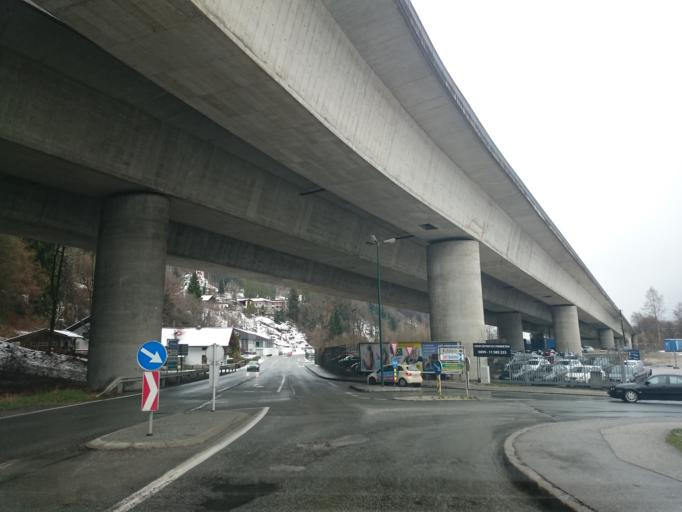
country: AT
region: Tyrol
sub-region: Politischer Bezirk Kufstein
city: Kufstein
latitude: 47.5893
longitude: 12.1629
